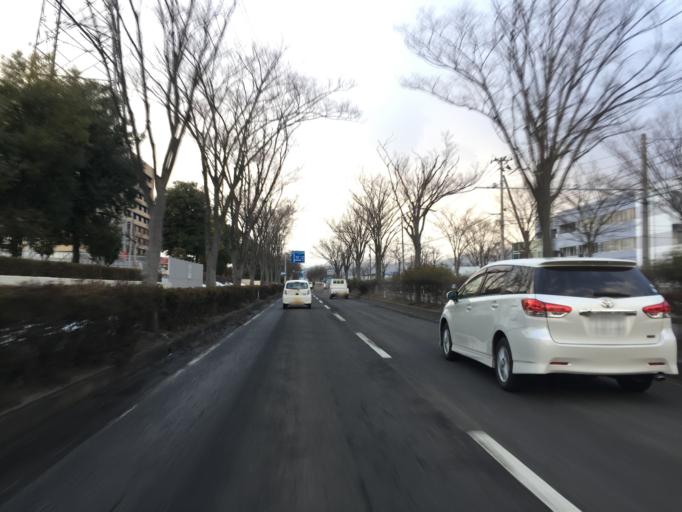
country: JP
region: Fukushima
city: Fukushima-shi
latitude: 37.7973
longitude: 140.4623
